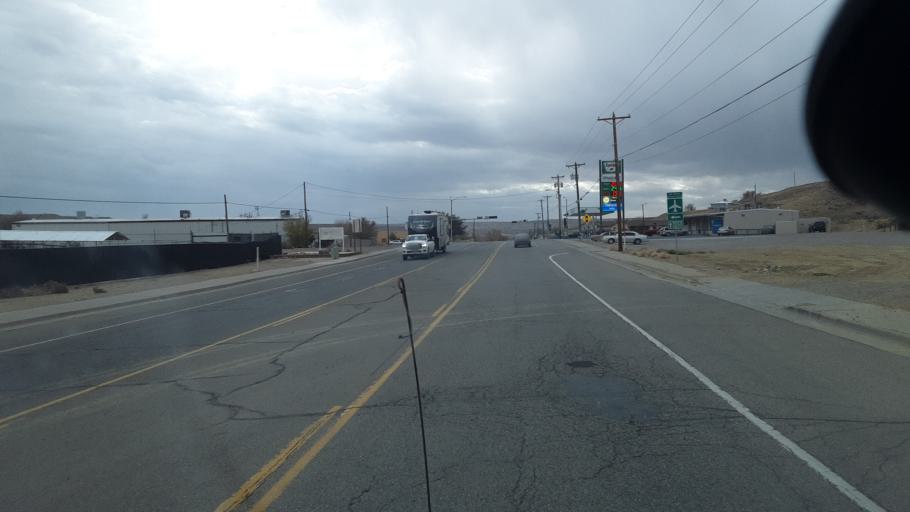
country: US
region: New Mexico
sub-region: San Juan County
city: Farmington
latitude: 36.7599
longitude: -108.2416
